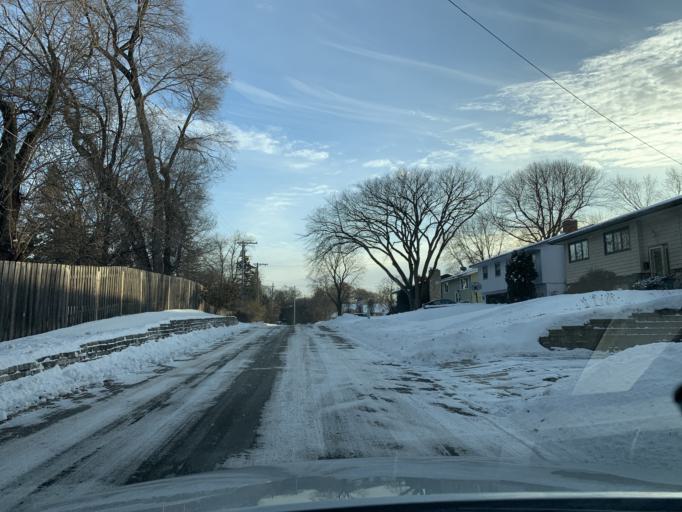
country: US
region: Minnesota
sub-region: Hennepin County
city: Minnetonka Mills
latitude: 44.9499
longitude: -93.3959
